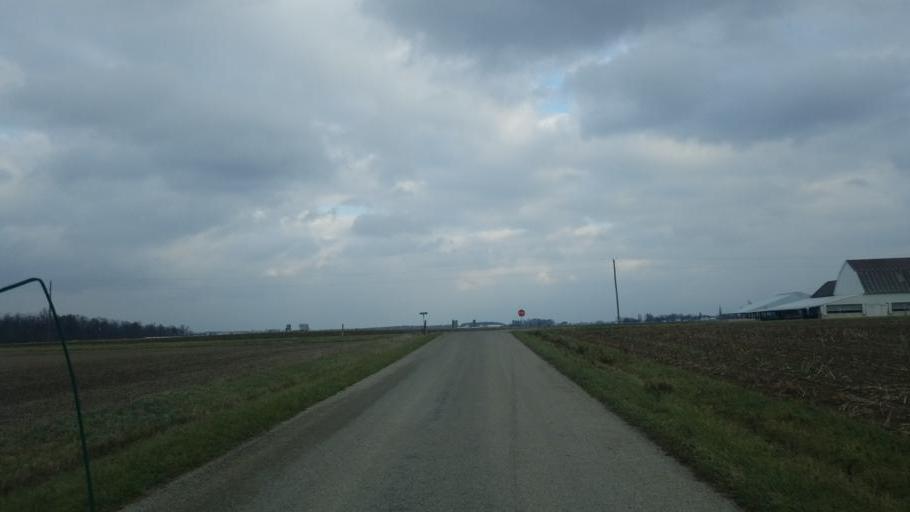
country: US
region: Ohio
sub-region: Mercer County
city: Fort Recovery
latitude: 40.5136
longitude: -84.8038
